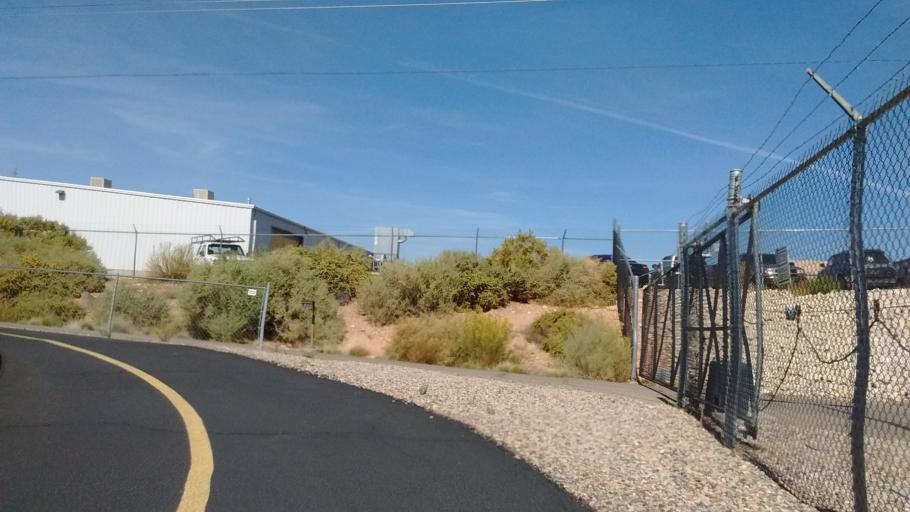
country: US
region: Utah
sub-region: Washington County
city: Washington
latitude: 37.1115
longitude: -113.5182
